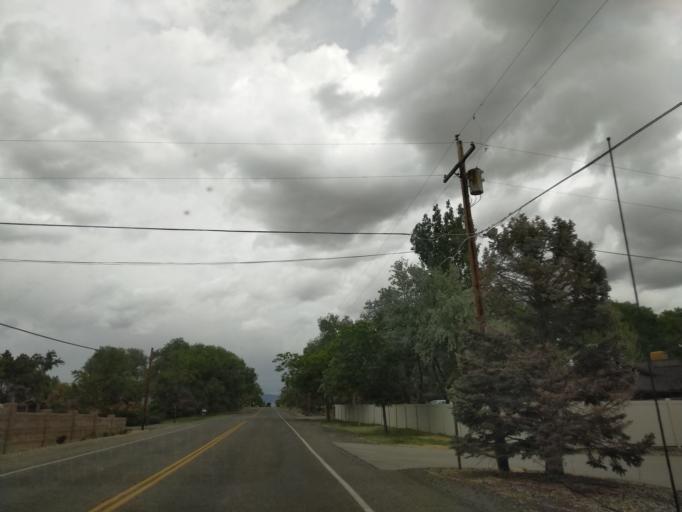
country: US
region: Colorado
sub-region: Mesa County
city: Grand Junction
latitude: 39.1035
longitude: -108.5616
